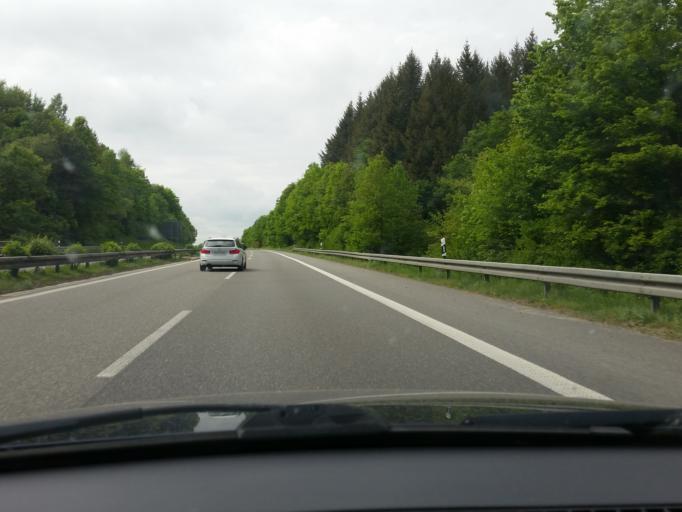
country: DE
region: Baden-Wuerttemberg
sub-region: Freiburg Region
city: Radolfzell am Bodensee
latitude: 47.7675
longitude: 8.9750
